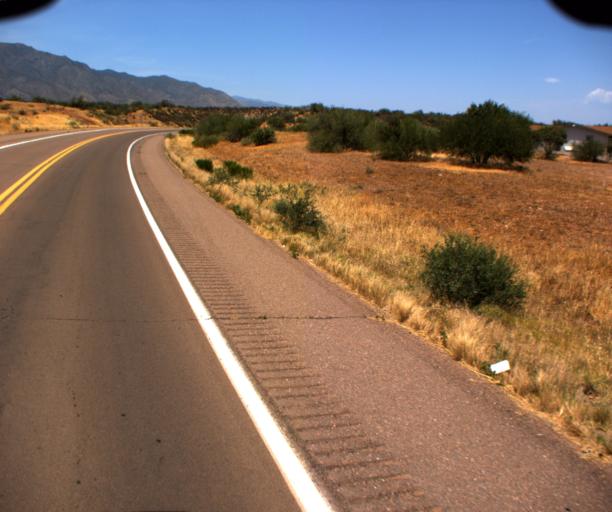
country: US
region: Arizona
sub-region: Gila County
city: Tonto Basin
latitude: 33.8616
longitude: -111.3122
